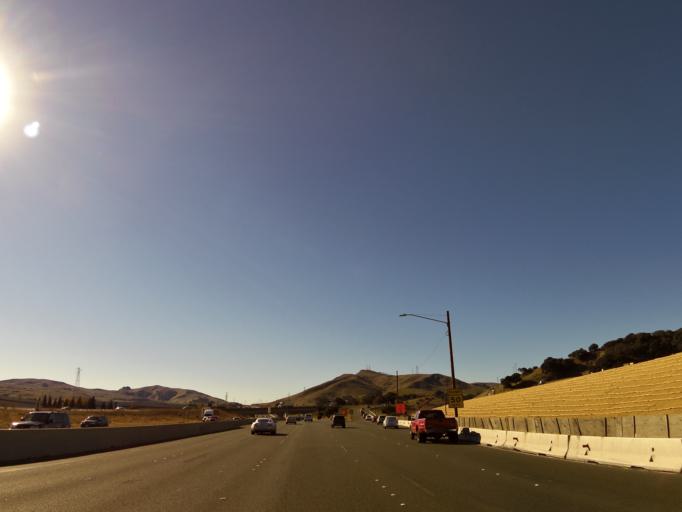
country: US
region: California
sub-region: Solano County
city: Green Valley
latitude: 38.2108
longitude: -122.1467
